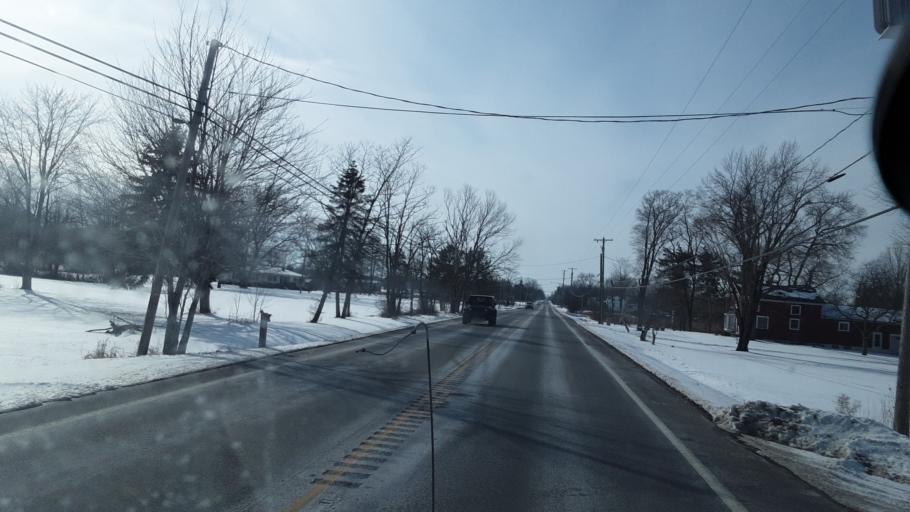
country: US
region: Ohio
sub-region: Stark County
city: Alliance
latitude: 41.0236
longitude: -81.1196
